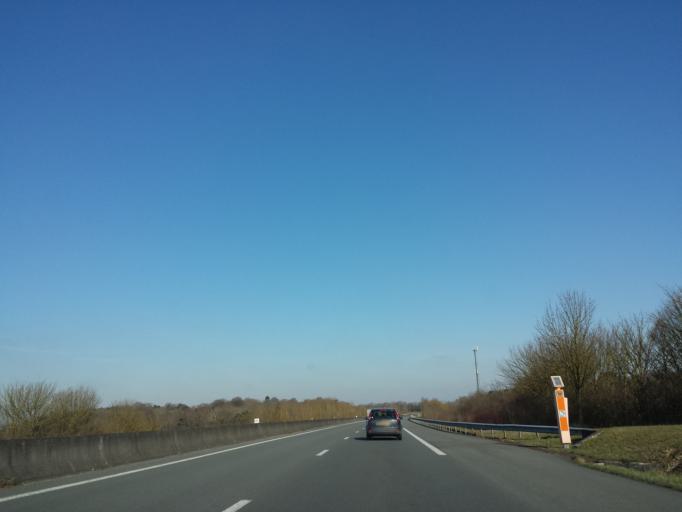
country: FR
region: Picardie
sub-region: Departement de la Somme
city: Saleux
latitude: 49.8129
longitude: 2.2440
